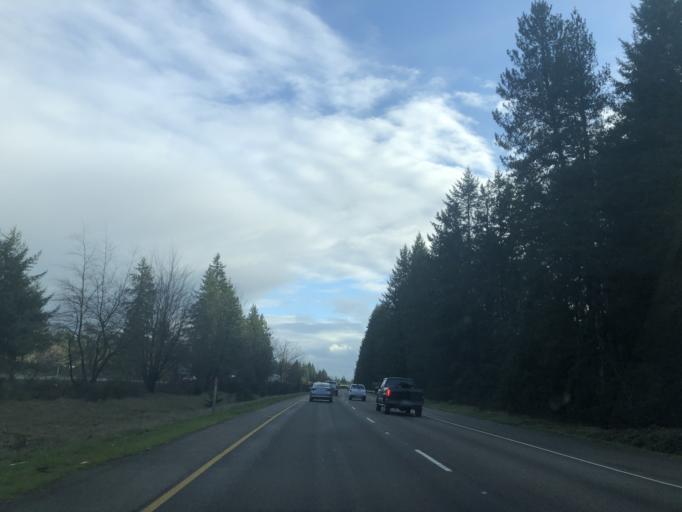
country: US
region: Washington
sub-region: Kitsap County
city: Bethel
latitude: 47.4910
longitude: -122.6361
